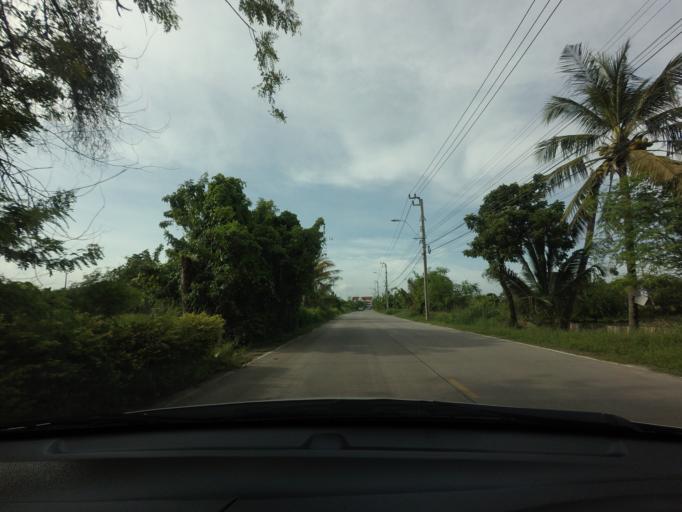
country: TH
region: Bangkok
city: Bang Na
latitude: 13.6329
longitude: 100.6644
